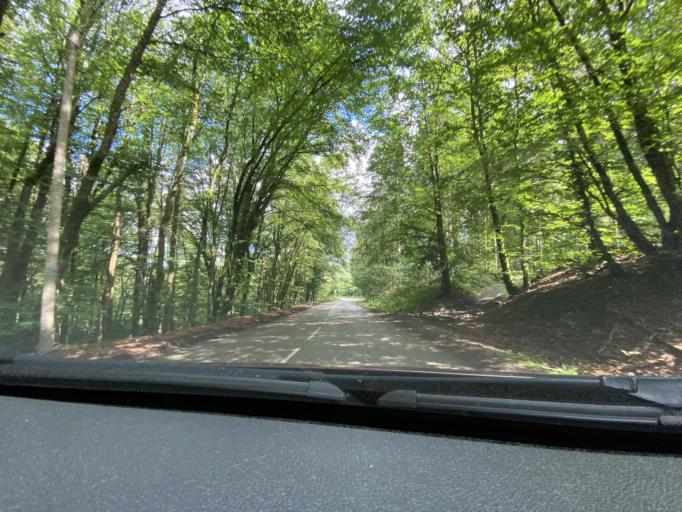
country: FR
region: Bourgogne
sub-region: Departement de la Cote-d'Or
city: Saulieu
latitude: 47.2580
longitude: 4.0765
